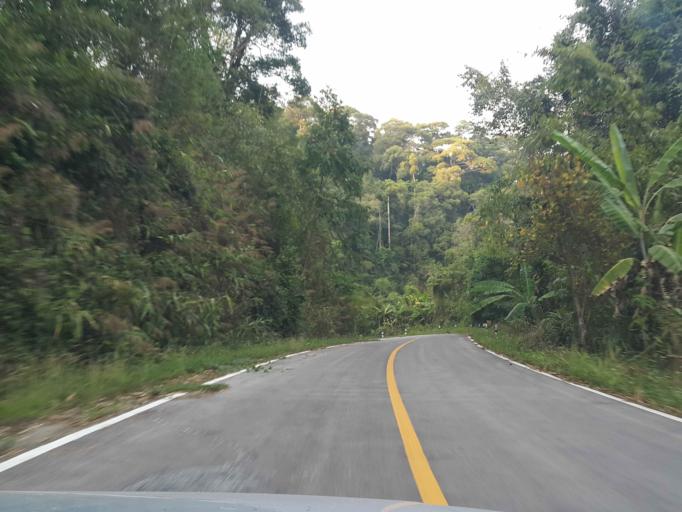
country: TH
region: Chiang Mai
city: Mae On
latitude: 18.9758
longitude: 99.3237
